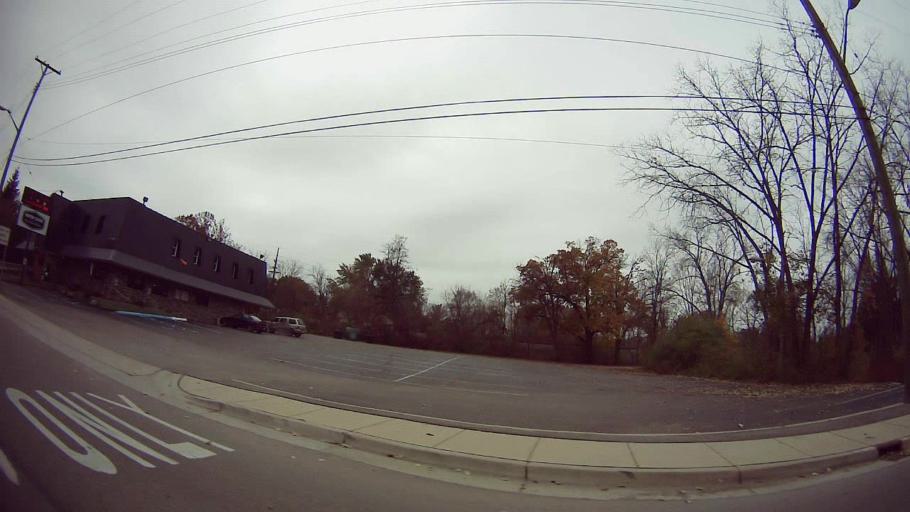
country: US
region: Michigan
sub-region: Oakland County
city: Waterford
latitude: 42.6803
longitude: -83.3723
